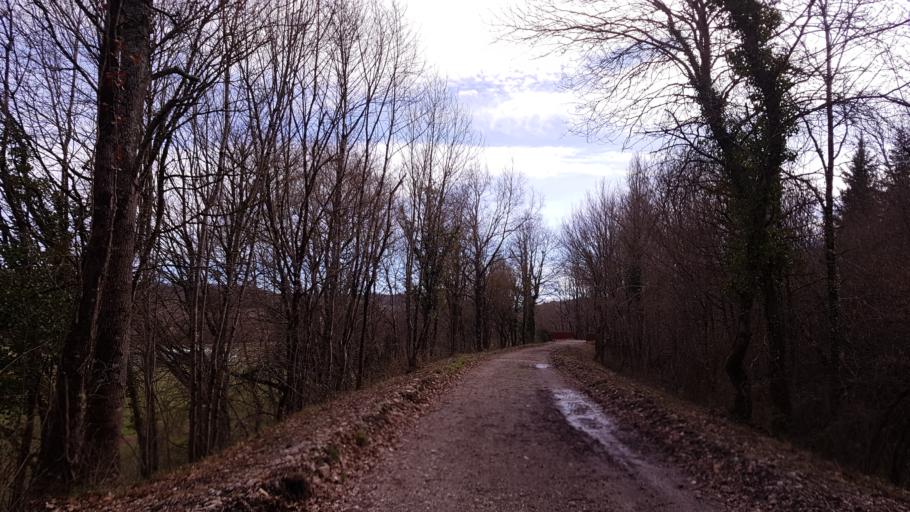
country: FR
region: Languedoc-Roussillon
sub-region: Departement de l'Aude
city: Chalabre
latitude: 43.0078
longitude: 1.9859
